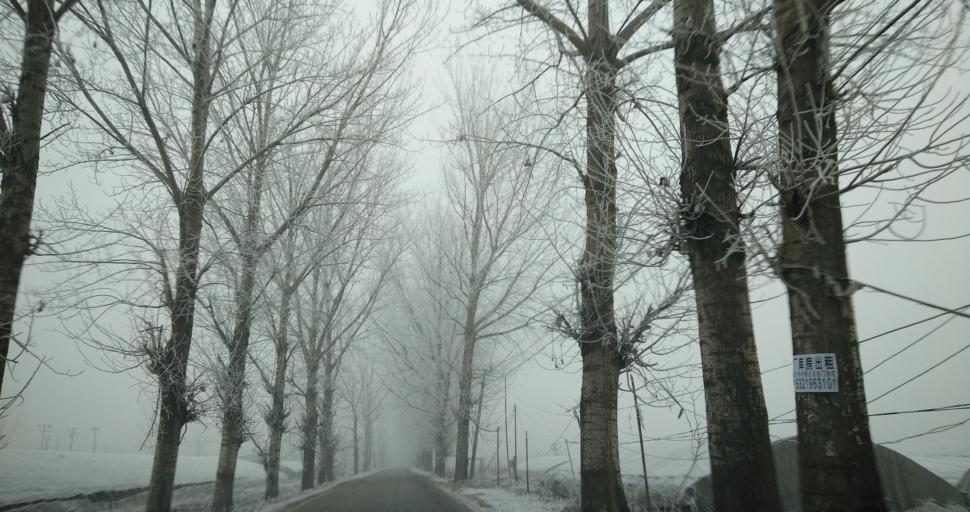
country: CN
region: Beijing
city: Yinghai
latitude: 39.7054
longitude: 116.4291
